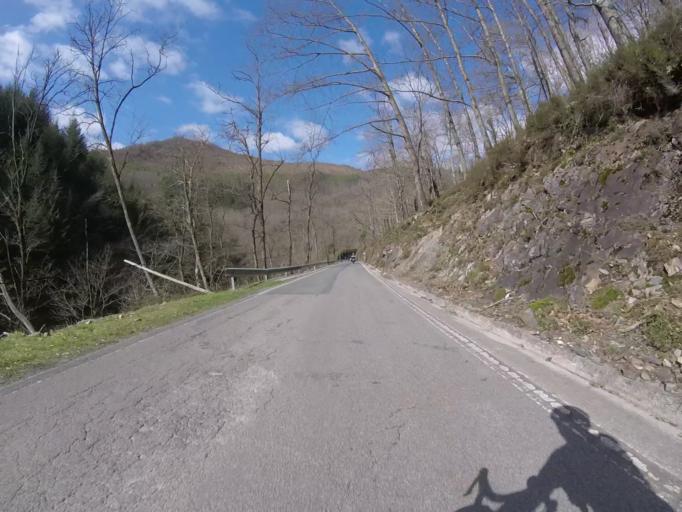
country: ES
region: Navarre
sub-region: Provincia de Navarra
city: Goizueta
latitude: 43.1552
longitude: -1.8492
